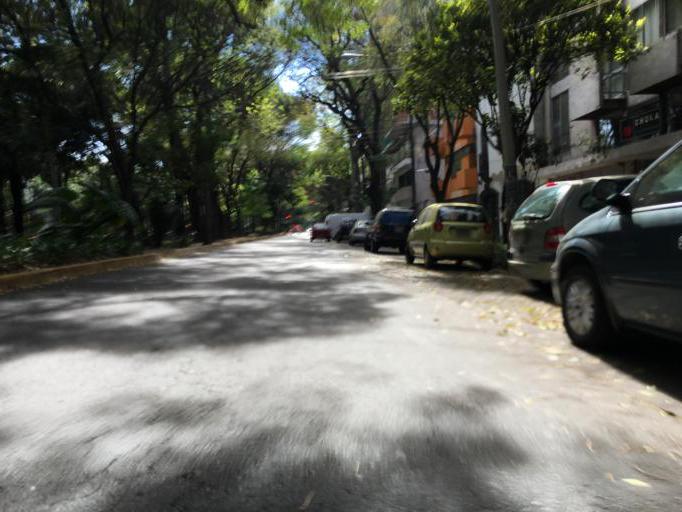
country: MX
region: Mexico City
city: Polanco
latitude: 19.4140
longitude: -99.1774
